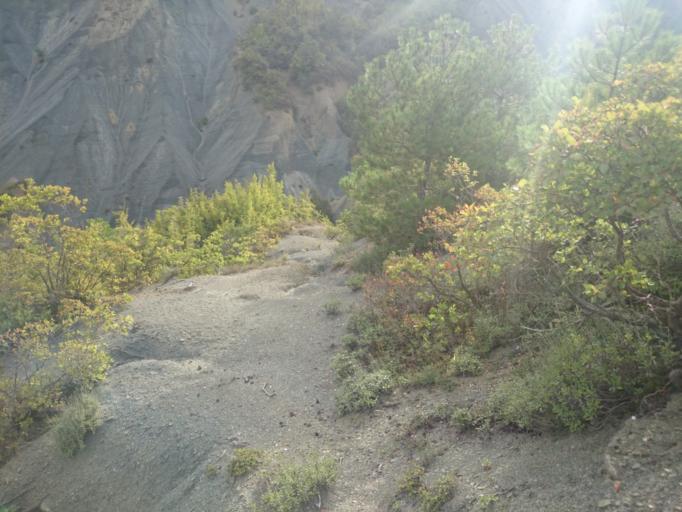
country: AL
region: Elbasan
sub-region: Rrethi i Gramshit
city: Kushove
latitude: 40.7582
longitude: 20.1923
